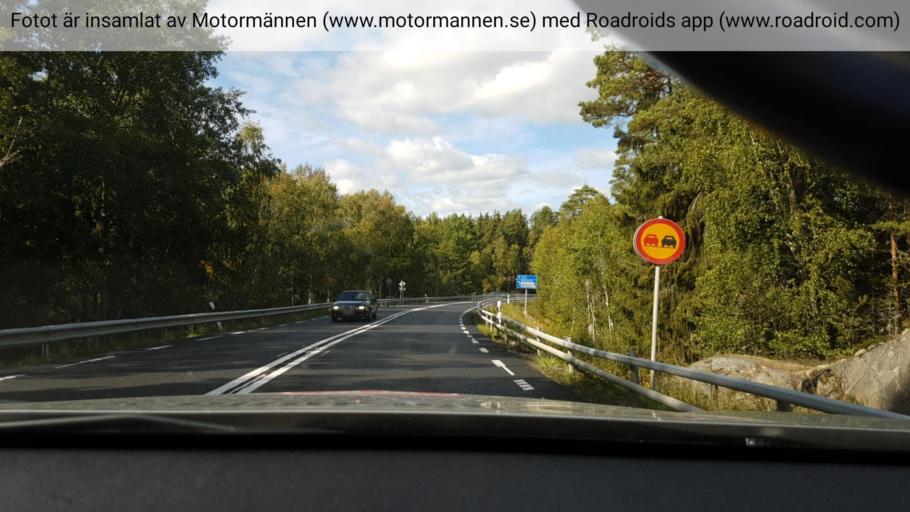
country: SE
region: Stockholm
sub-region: Lidingo
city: Brevik
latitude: 59.4284
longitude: 18.2240
